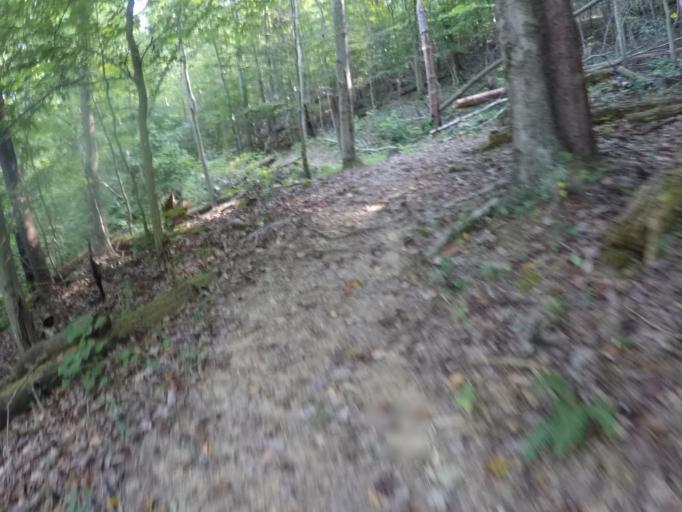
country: US
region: Ohio
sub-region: Lawrence County
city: Ironton
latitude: 38.6159
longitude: -82.6270
